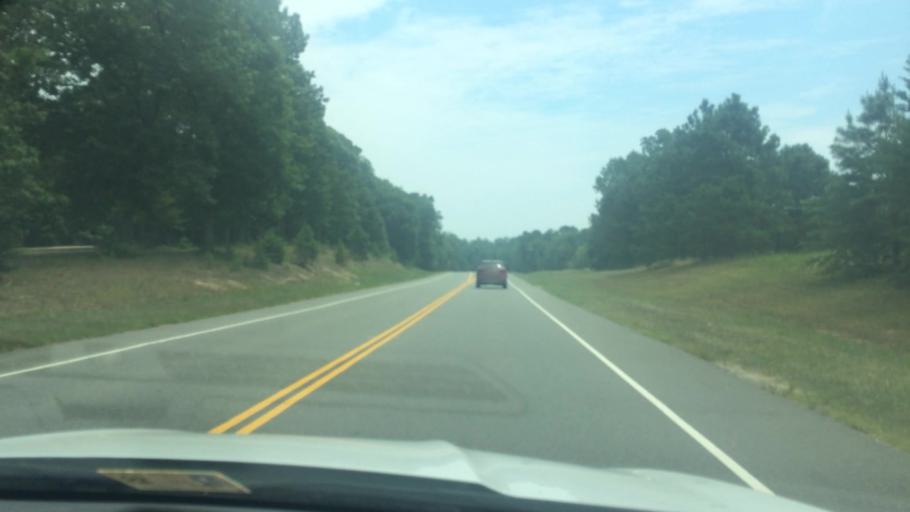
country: US
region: Virginia
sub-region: James City County
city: Williamsburg
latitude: 37.2634
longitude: -76.7922
